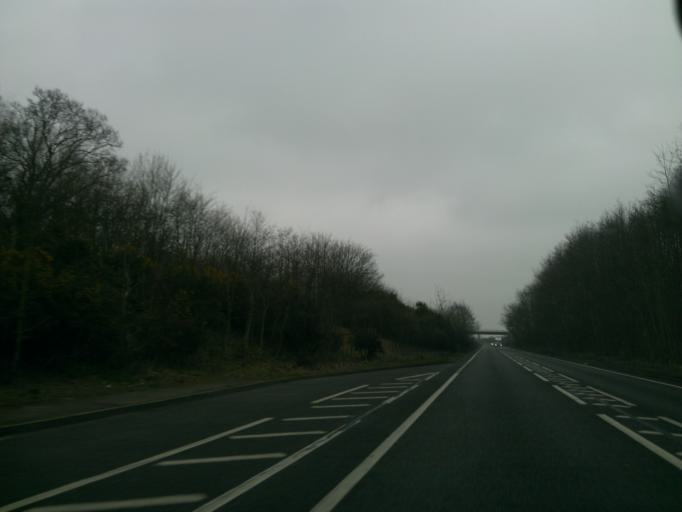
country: GB
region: England
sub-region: Essex
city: Little Clacton
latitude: 51.8451
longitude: 1.1080
